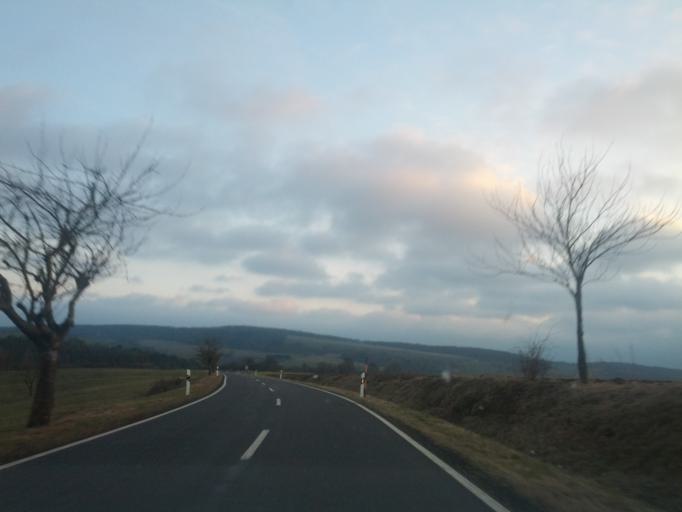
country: DE
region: Thuringia
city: Heyerode
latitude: 51.1814
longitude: 10.2939
